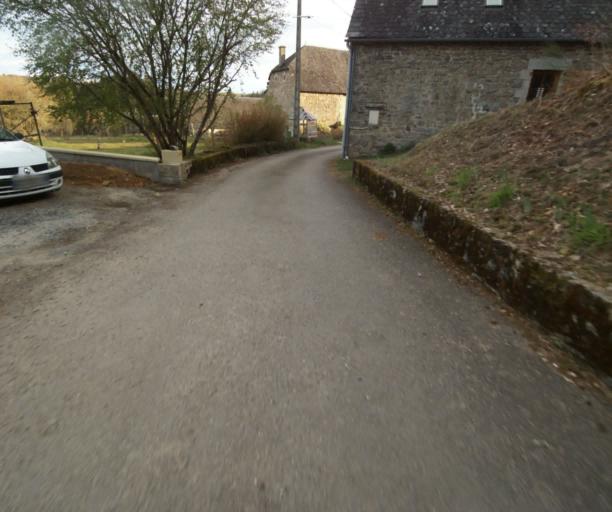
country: FR
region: Limousin
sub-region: Departement de la Correze
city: Argentat
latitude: 45.2216
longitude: 1.9802
